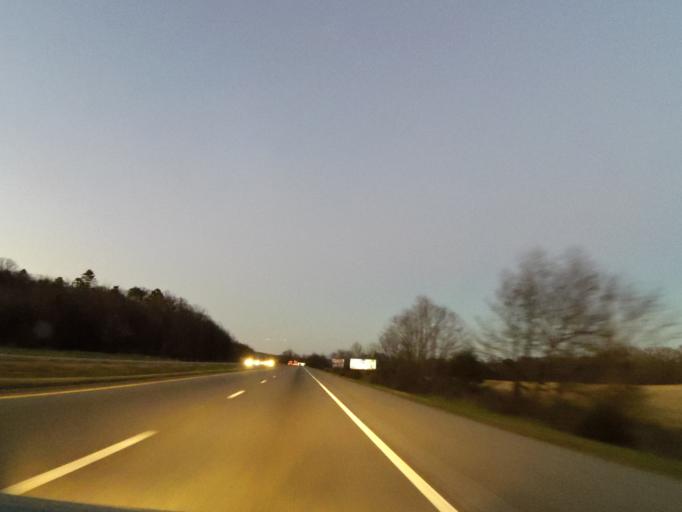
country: US
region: Tennessee
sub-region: Cocke County
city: Newport
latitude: 35.8946
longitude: -83.1852
